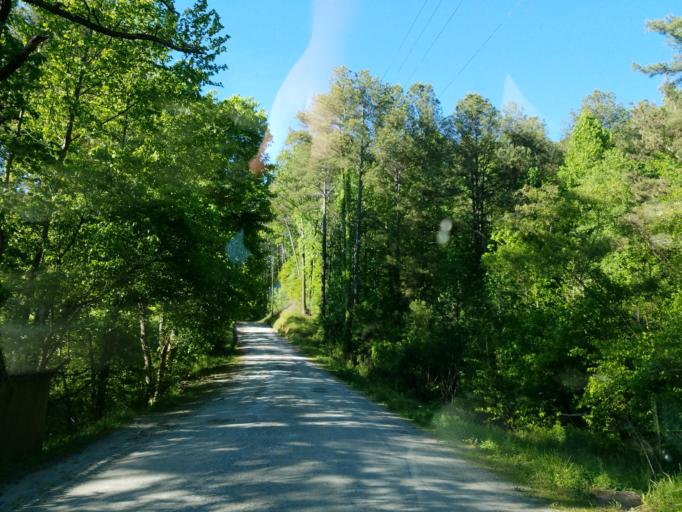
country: US
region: Georgia
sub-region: Gilmer County
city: Ellijay
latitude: 34.6106
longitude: -84.5040
